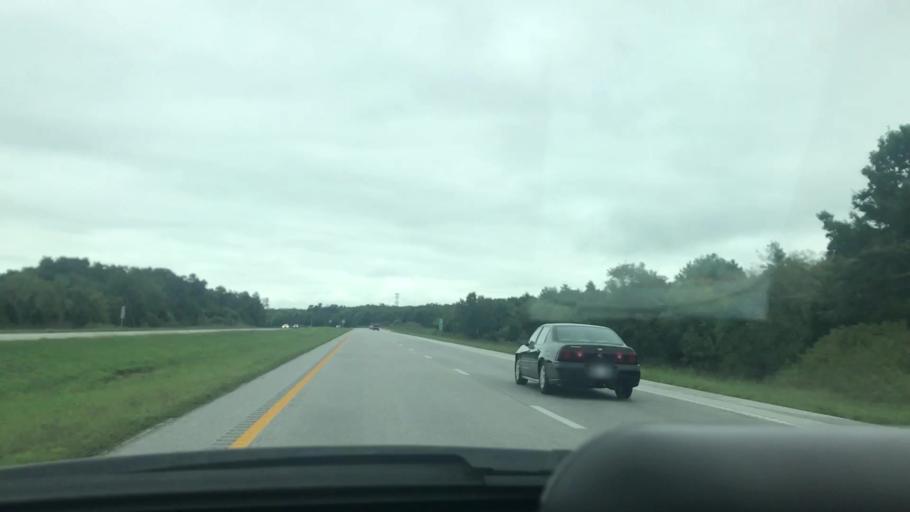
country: US
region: Missouri
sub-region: Greene County
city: Fair Grove
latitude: 37.3162
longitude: -93.1700
